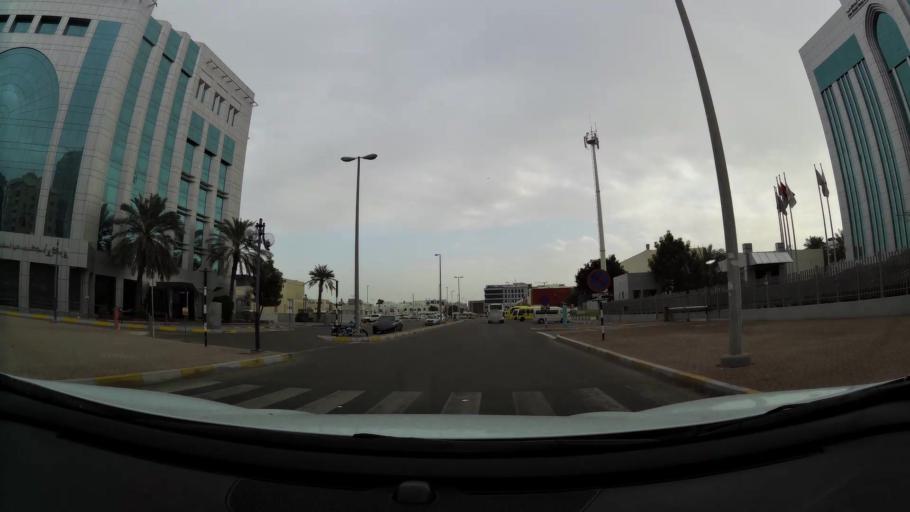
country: AE
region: Abu Dhabi
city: Abu Dhabi
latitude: 24.4835
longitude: 54.3778
